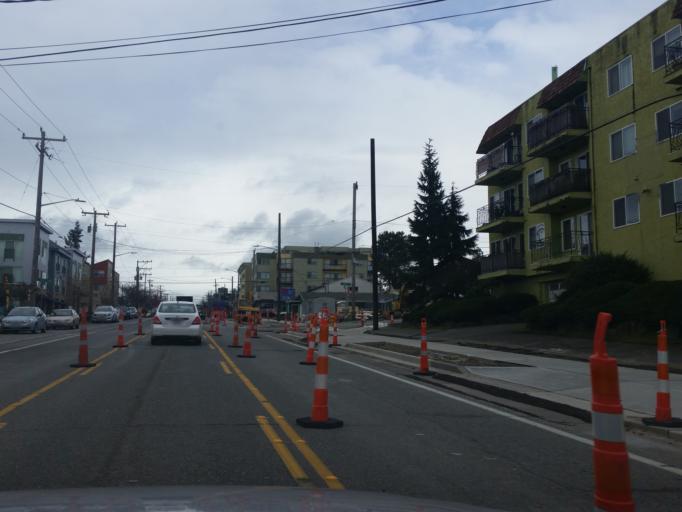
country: US
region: Washington
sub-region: King County
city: Shoreline
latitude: 47.7024
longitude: -122.3554
